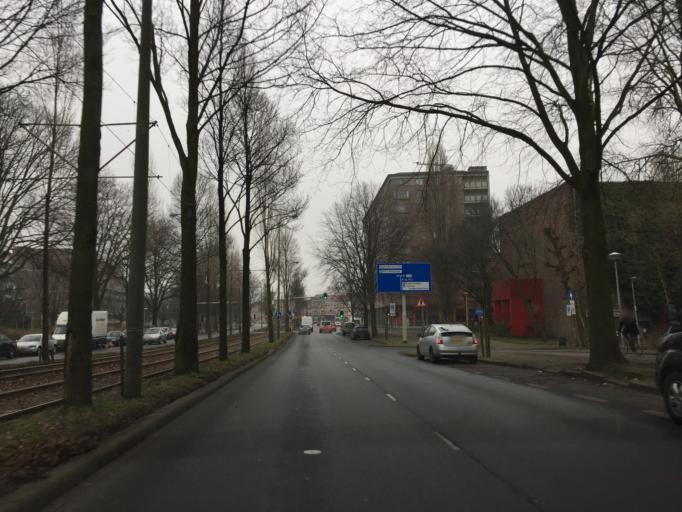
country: NL
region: South Holland
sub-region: Gemeente Den Haag
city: The Hague
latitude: 52.0758
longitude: 4.2948
